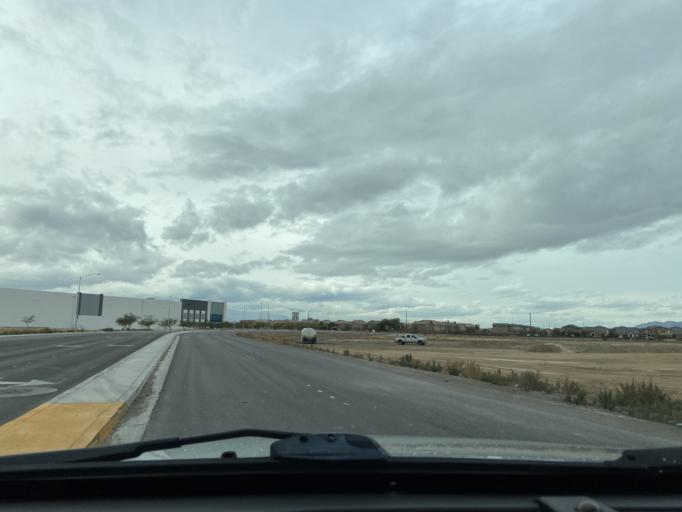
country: US
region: Nevada
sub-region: Clark County
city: Nellis Air Force Base
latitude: 36.2620
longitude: -115.0802
